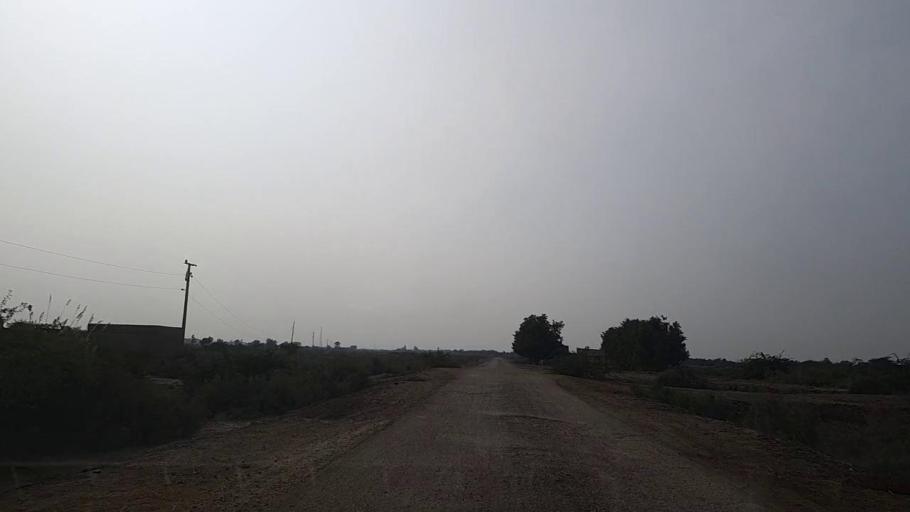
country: PK
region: Sindh
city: Mirpur Sakro
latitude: 24.6438
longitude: 67.6083
